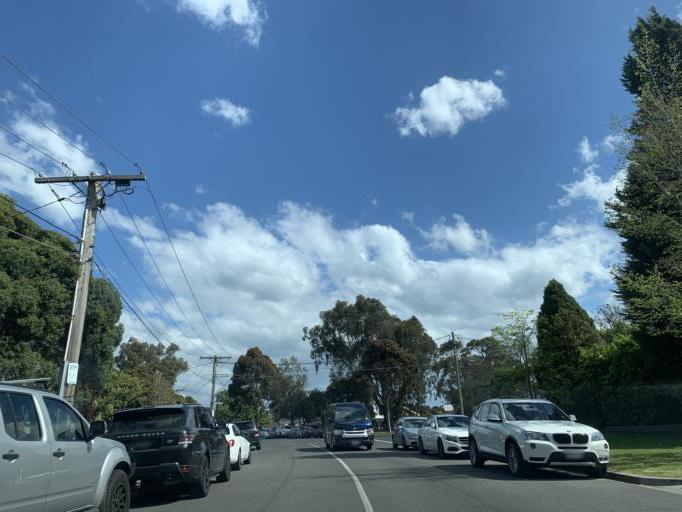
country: AU
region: Victoria
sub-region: Bayside
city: North Brighton
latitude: -37.9081
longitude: 144.9958
